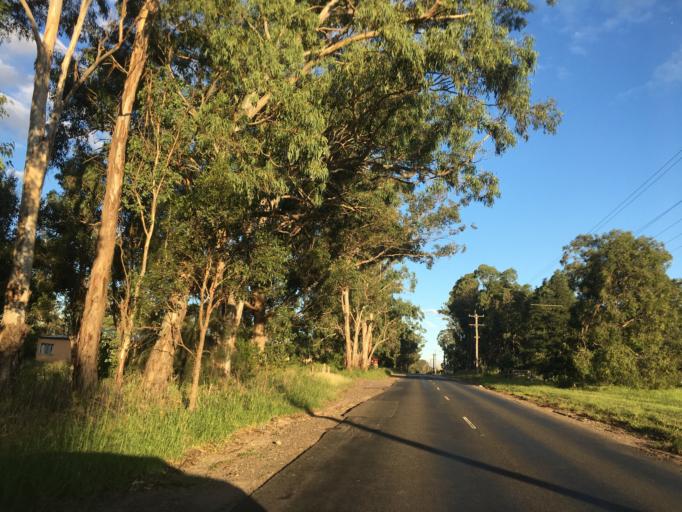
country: AU
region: New South Wales
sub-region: Campbelltown Municipality
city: Denham Court
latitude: -33.9646
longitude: 150.8086
